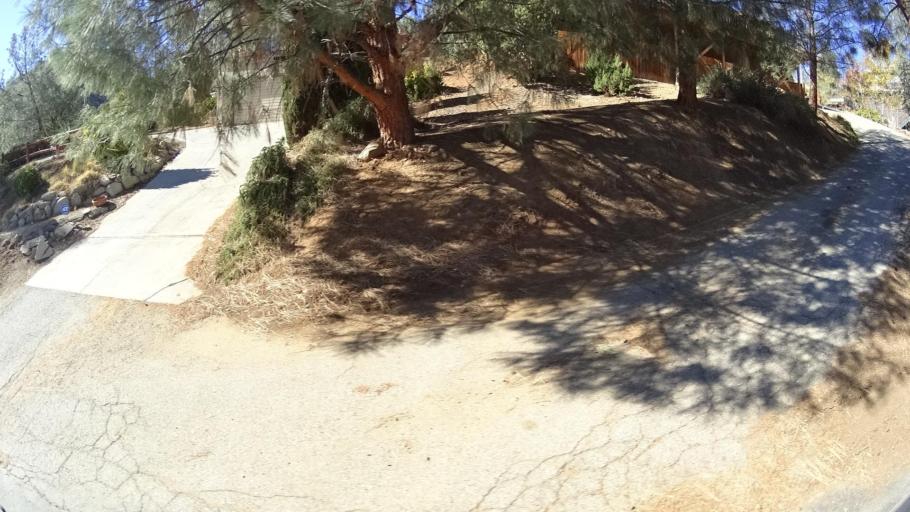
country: US
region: California
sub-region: Kern County
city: Wofford Heights
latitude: 35.7047
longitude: -118.4654
